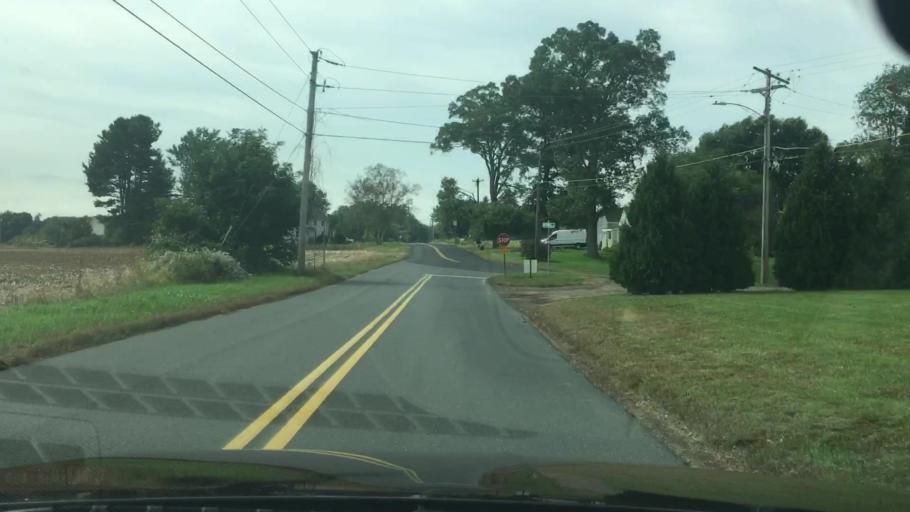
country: US
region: Connecticut
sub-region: Hartford County
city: Broad Brook
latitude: 41.8948
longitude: -72.5267
